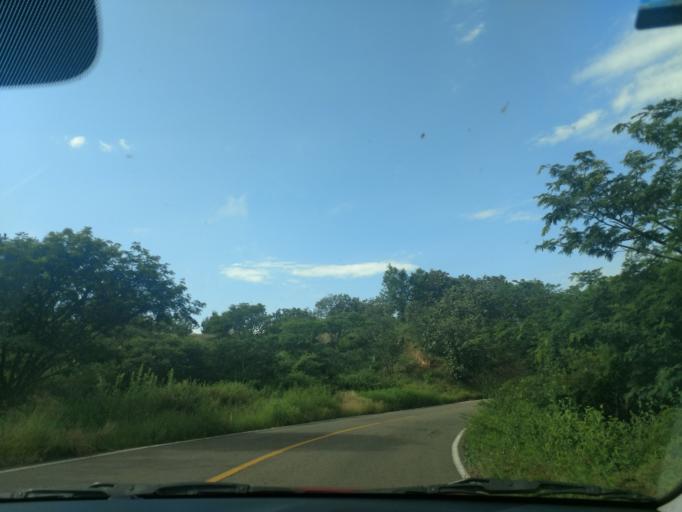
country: MX
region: Jalisco
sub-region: Atengo
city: Soyatlan del Oro
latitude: 20.4999
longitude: -104.3543
